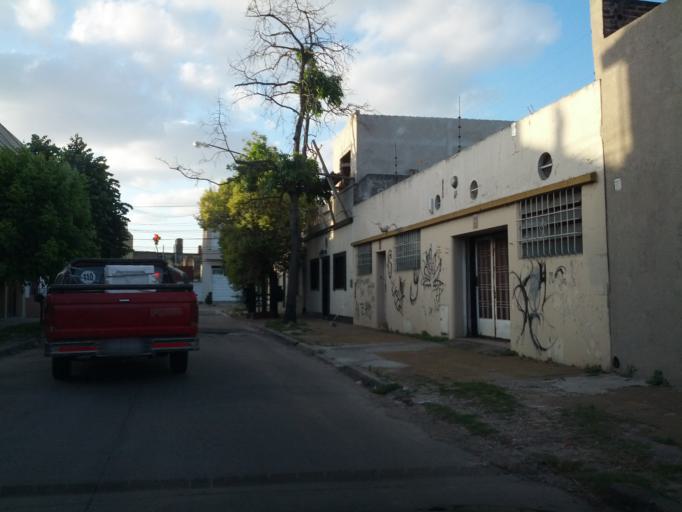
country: AR
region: Buenos Aires
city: San Justo
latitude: -34.6500
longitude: -58.5303
